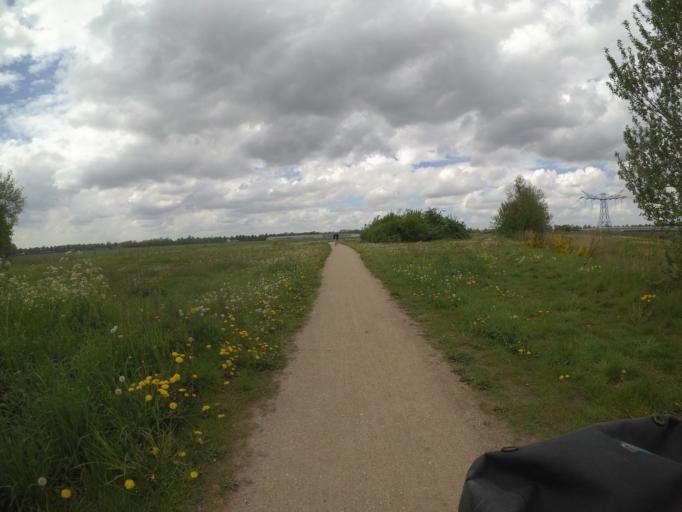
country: NL
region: North Brabant
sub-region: Gemeente Dongen
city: Dongen
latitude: 51.6310
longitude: 4.9626
